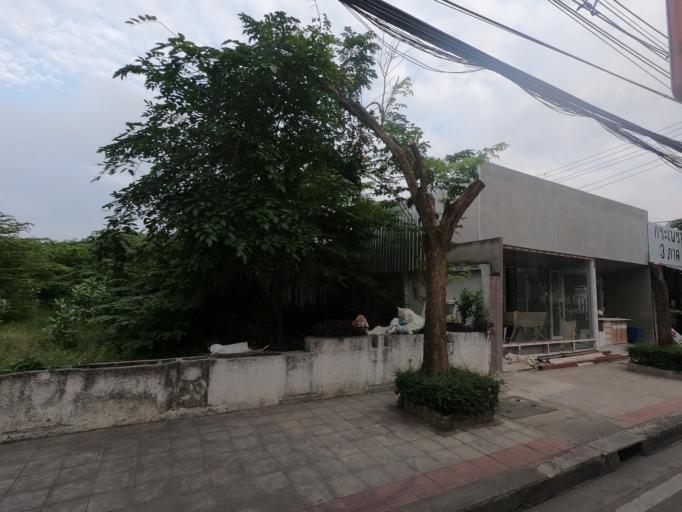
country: TH
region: Bangkok
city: Lat Phrao
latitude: 13.7977
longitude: 100.6069
